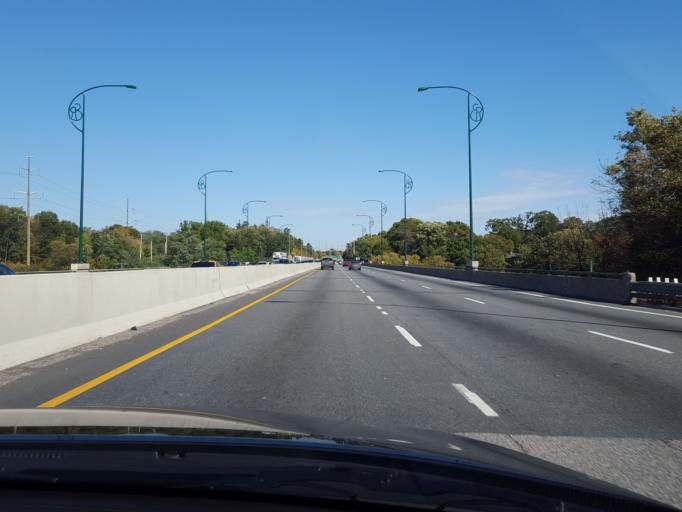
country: CA
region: Ontario
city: Mississauga
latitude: 43.5551
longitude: -79.6110
